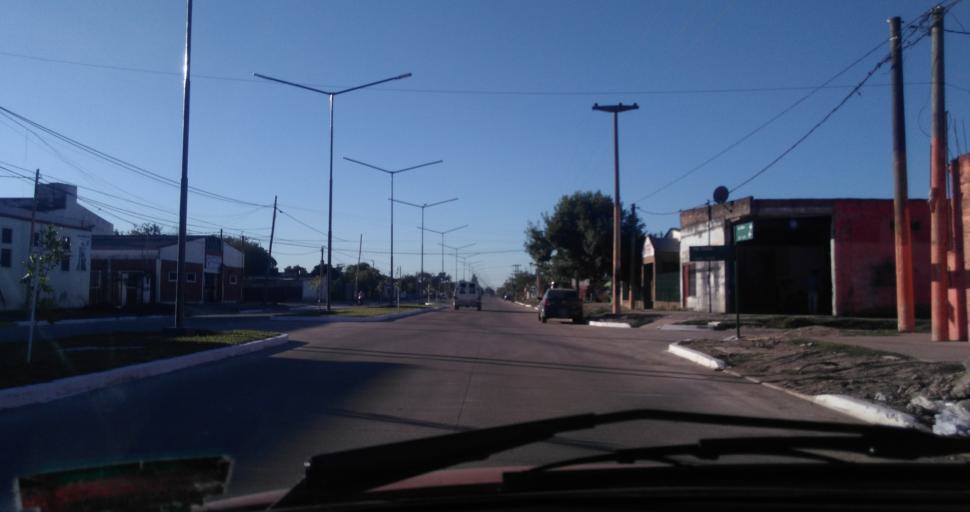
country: AR
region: Chaco
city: Resistencia
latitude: -27.4806
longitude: -58.9820
